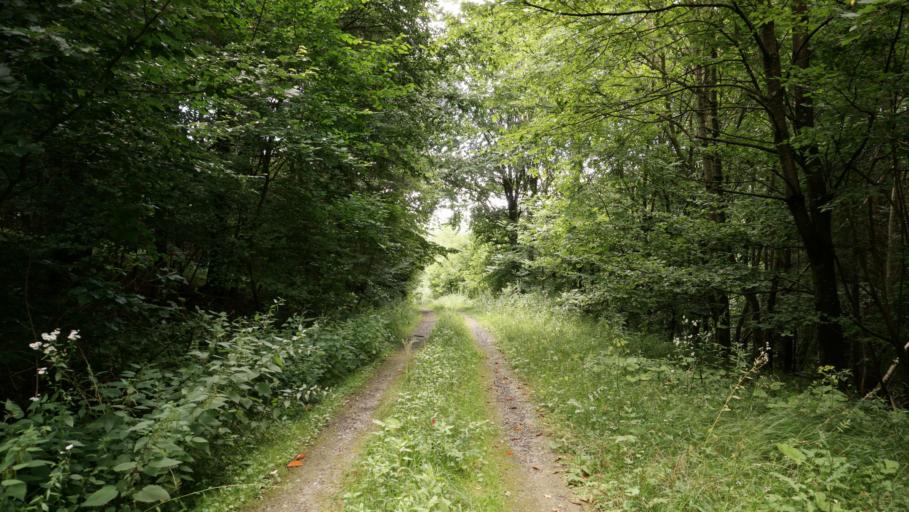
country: DE
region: Baden-Wuerttemberg
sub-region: Karlsruhe Region
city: Neckarzimmern
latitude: 49.3227
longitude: 9.1523
